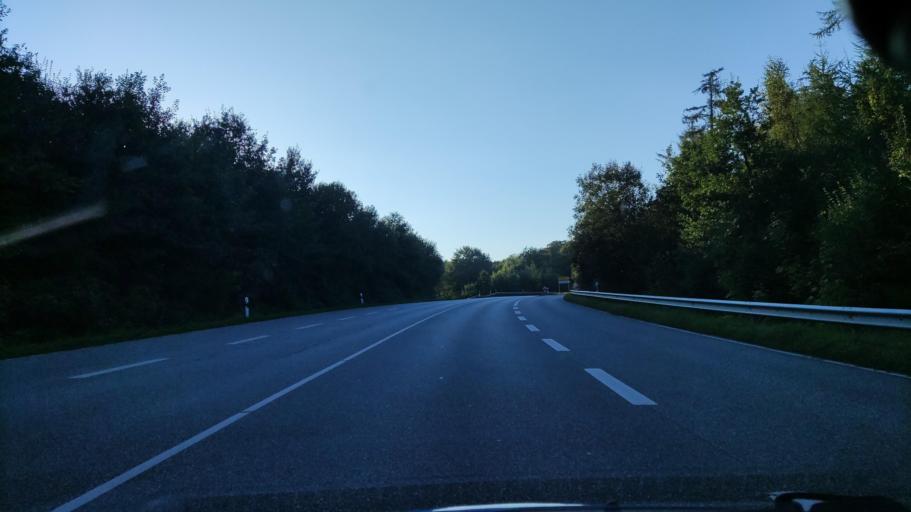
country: DE
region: Schleswig-Holstein
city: Preetz
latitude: 54.2479
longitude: 10.2797
